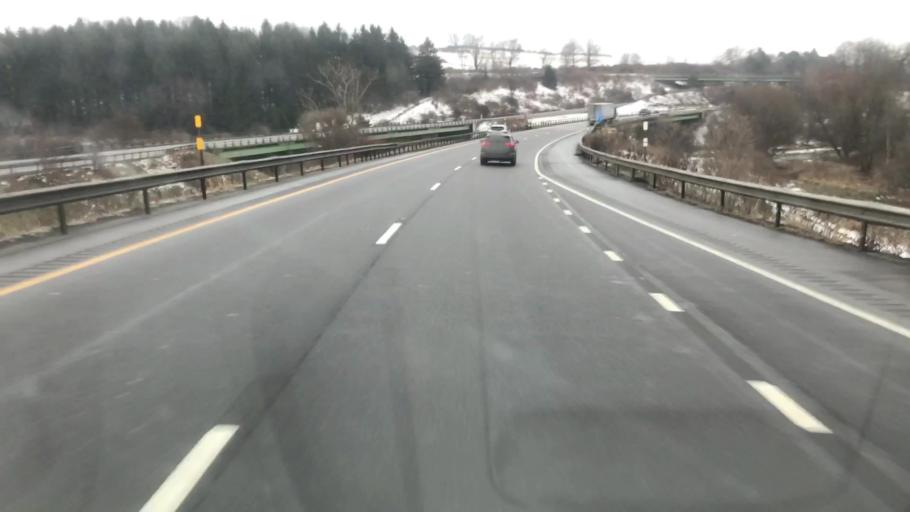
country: US
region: New York
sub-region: Cortland County
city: Cortland
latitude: 42.6078
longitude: -76.1593
